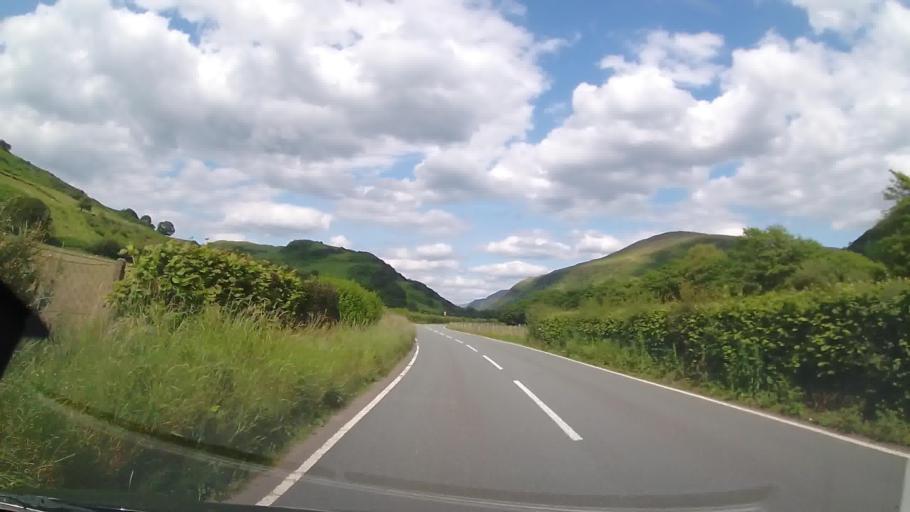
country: GB
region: Wales
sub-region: Gwynedd
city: Tywyn
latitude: 52.6198
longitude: -4.0092
